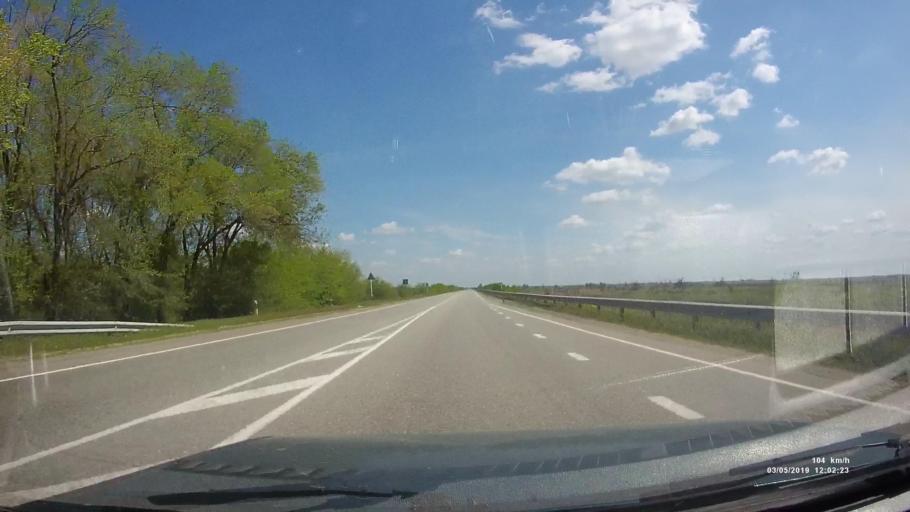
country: RU
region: Rostov
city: Bagayevskaya
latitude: 47.2708
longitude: 40.3674
